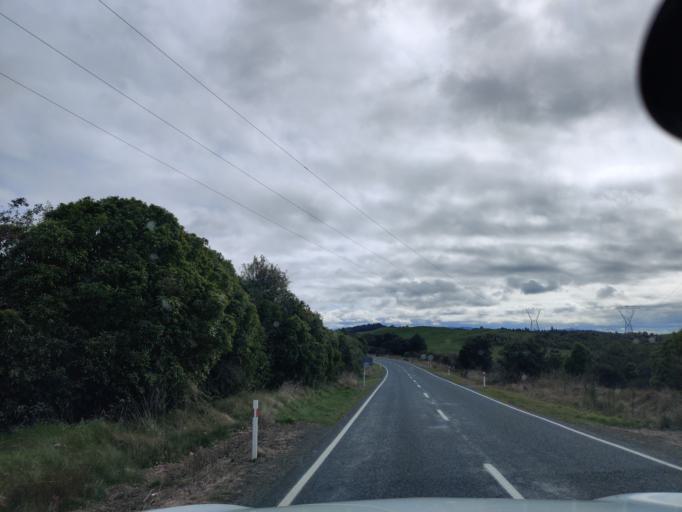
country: NZ
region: Waikato
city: Turangi
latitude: -38.8008
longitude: 175.6862
